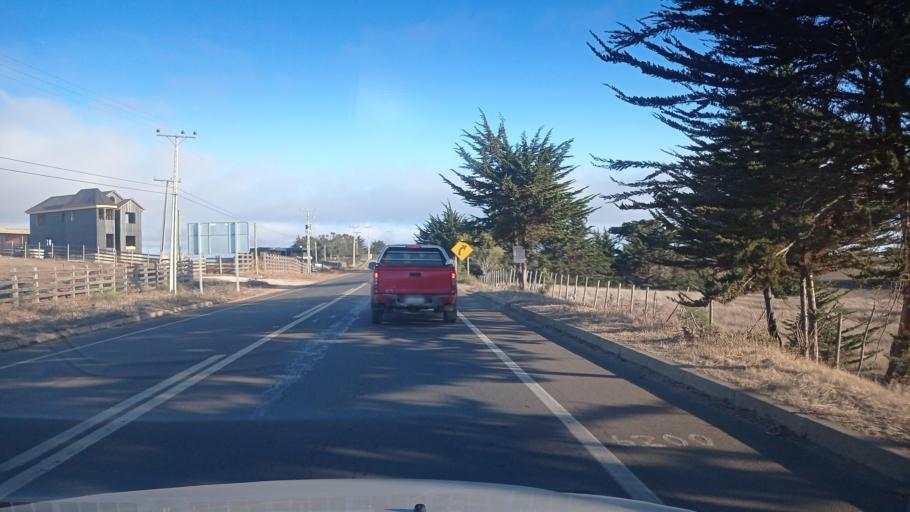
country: CL
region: O'Higgins
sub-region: Provincia de Colchagua
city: Santa Cruz
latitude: -34.4369
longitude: -72.0328
